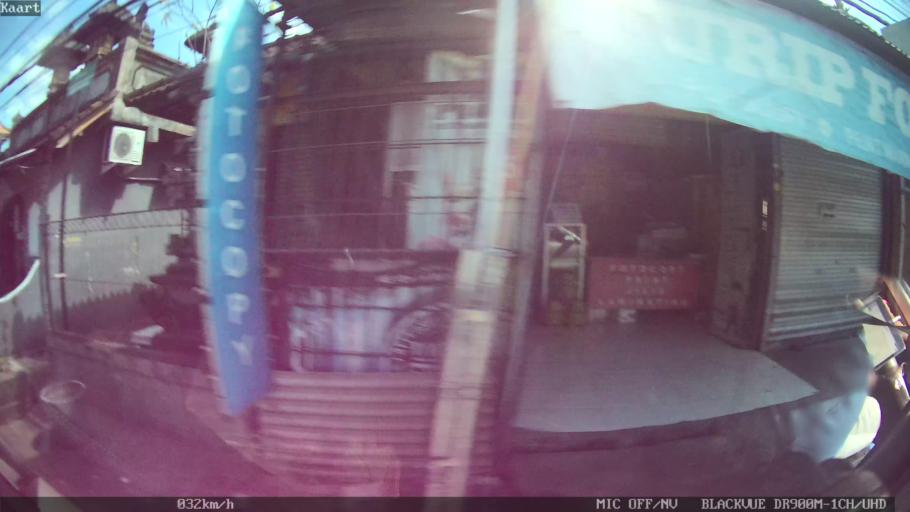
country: ID
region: Bali
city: Banjar Kertasari
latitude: -8.6336
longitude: 115.1842
